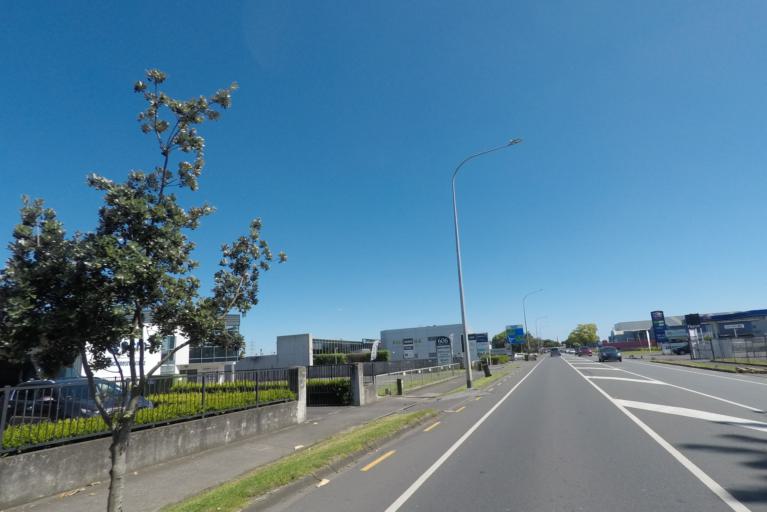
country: NZ
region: Auckland
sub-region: Auckland
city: Rosebank
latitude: -36.8750
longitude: 174.6697
